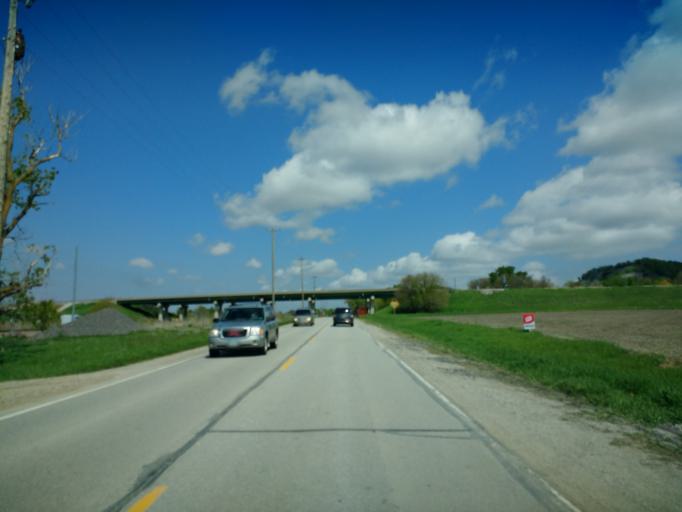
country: US
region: Iowa
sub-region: Harrison County
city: Missouri Valley
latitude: 41.4936
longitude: -95.8906
